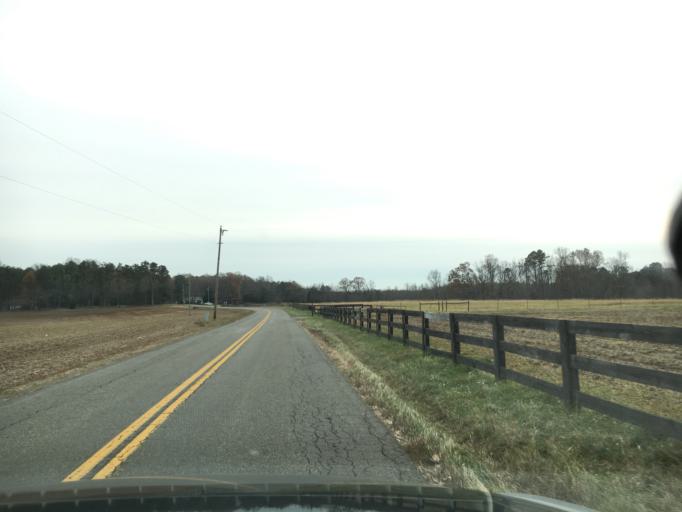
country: US
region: Virginia
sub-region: Henrico County
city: Wyndham
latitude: 37.7131
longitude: -77.6843
